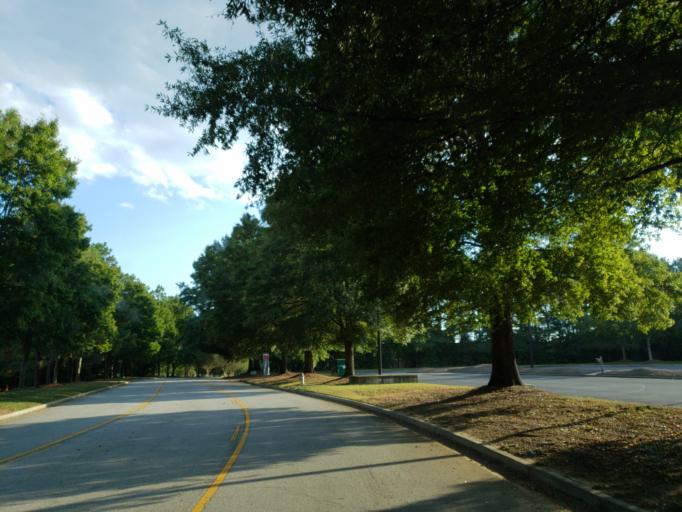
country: US
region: Georgia
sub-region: Cobb County
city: Mableton
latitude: 33.7660
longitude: -84.5620
